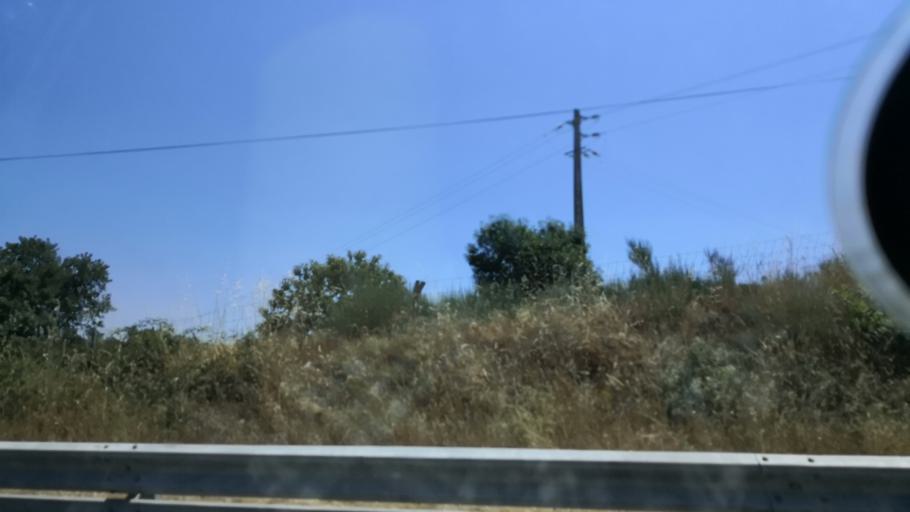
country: PT
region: Braganca
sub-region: Braganca Municipality
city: Braganca
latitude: 41.7658
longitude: -6.7919
